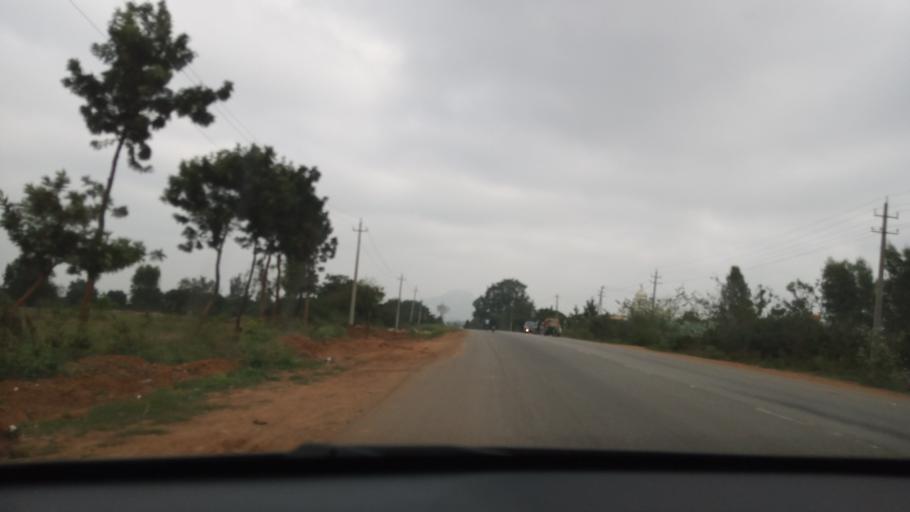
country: IN
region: Karnataka
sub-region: Chikkaballapur
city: Sidlaghatta
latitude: 13.2897
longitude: 77.9633
